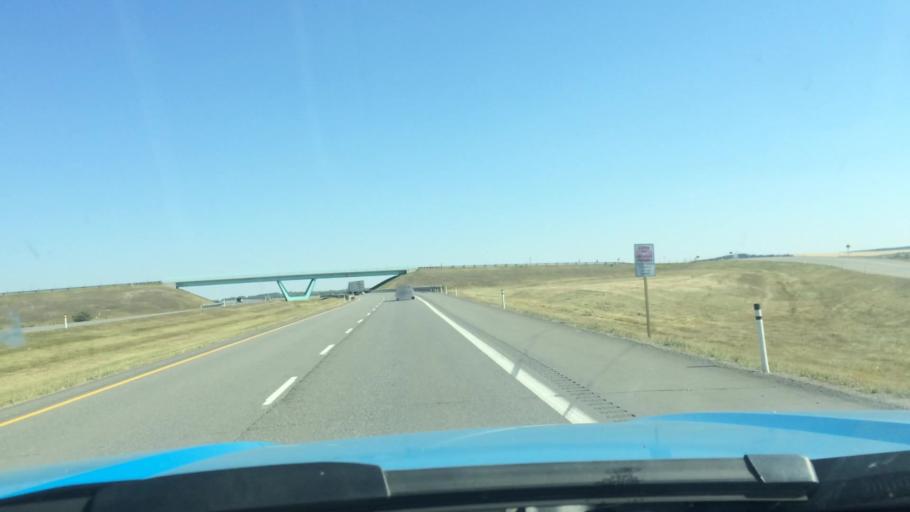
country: CA
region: Alberta
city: Cochrane
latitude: 51.0894
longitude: -114.5391
